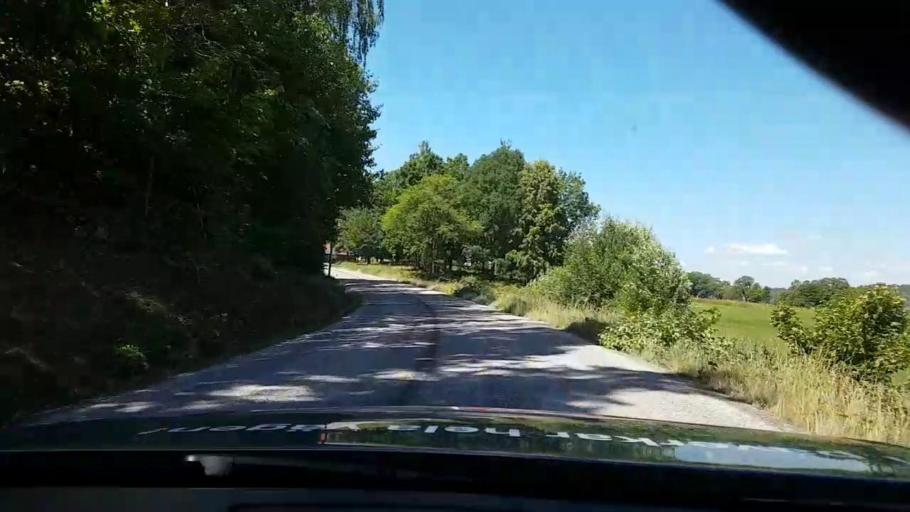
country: SE
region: Kalmar
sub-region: Vasterviks Kommun
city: Forserum
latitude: 57.9189
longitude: 16.6211
